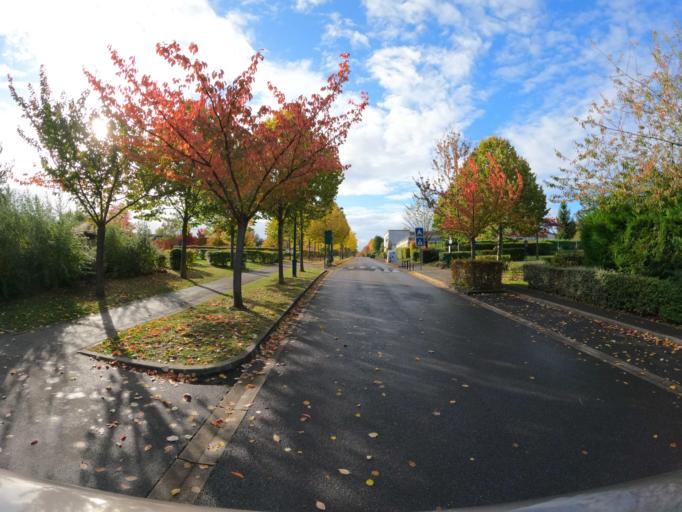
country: FR
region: Ile-de-France
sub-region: Departement de Seine-et-Marne
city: Magny-le-Hongre
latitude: 48.8642
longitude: 2.8234
